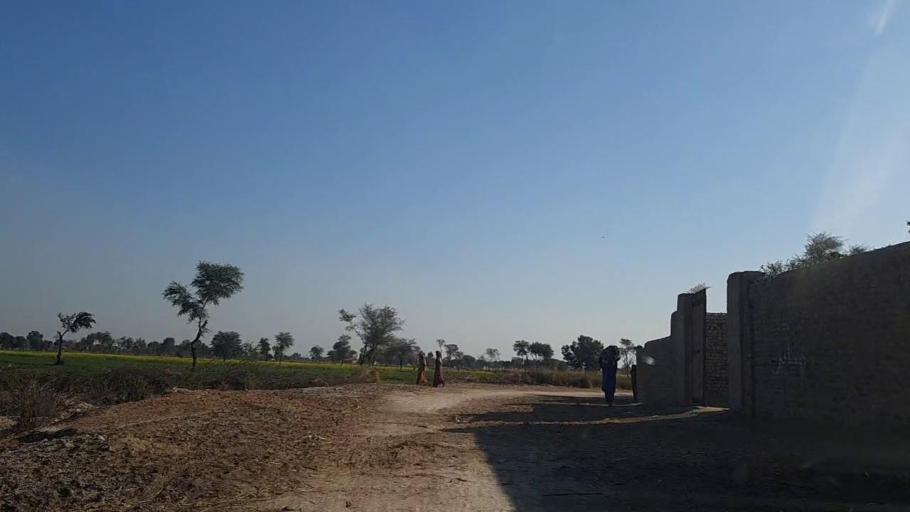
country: PK
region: Sindh
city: Daur
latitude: 26.3169
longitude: 68.1792
